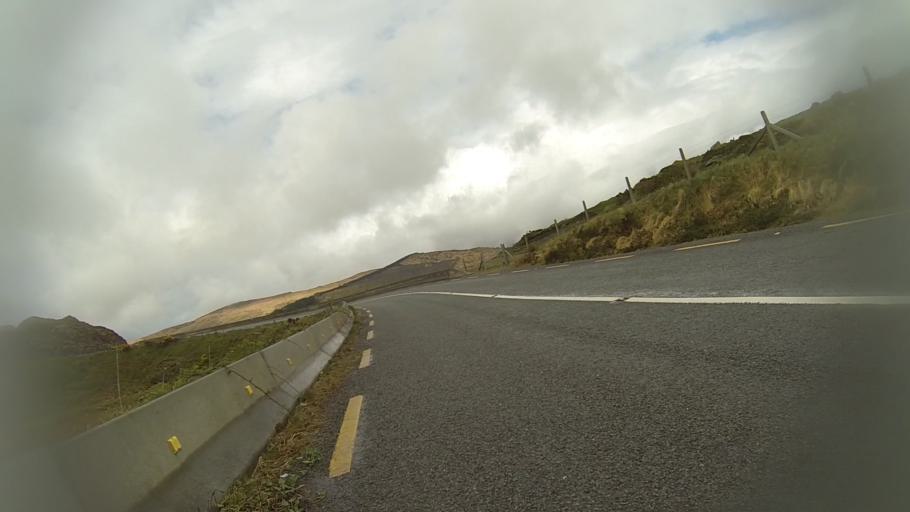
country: IE
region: Munster
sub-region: Ciarrai
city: Kenmare
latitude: 51.7962
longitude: -9.5849
